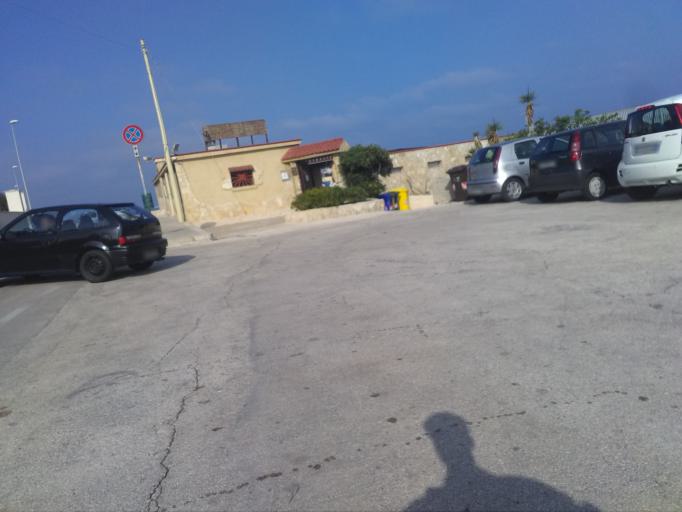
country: IT
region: Apulia
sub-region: Provincia di Bari
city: San Paolo
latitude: 41.1610
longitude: 16.7624
